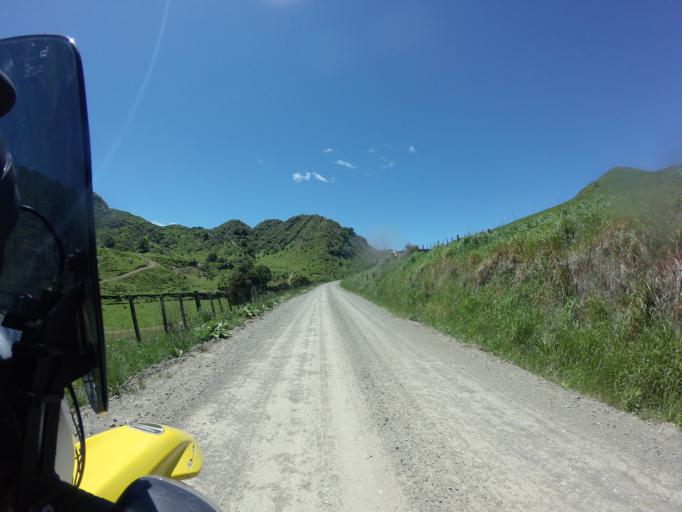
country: NZ
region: Bay of Plenty
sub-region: Opotiki District
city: Opotiki
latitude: -38.3883
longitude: 177.4612
